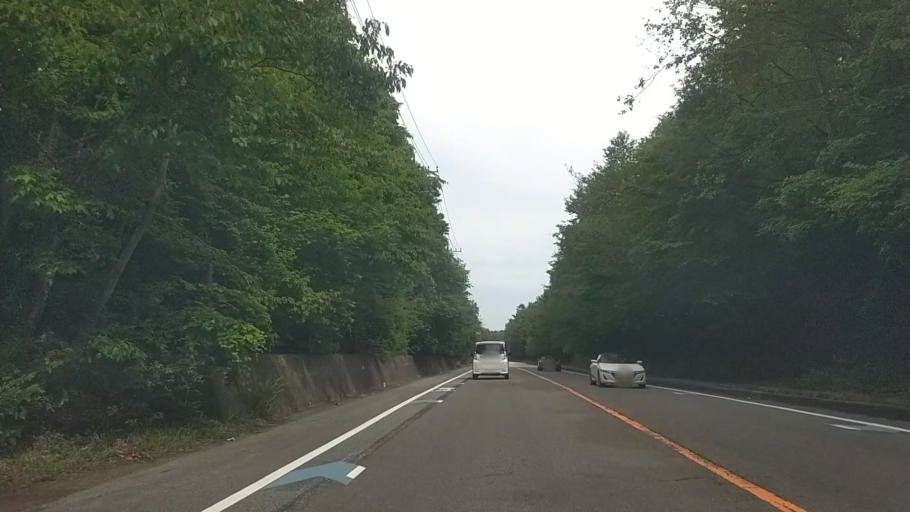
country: JP
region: Yamanashi
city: Fujikawaguchiko
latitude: 35.4879
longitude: 138.6274
